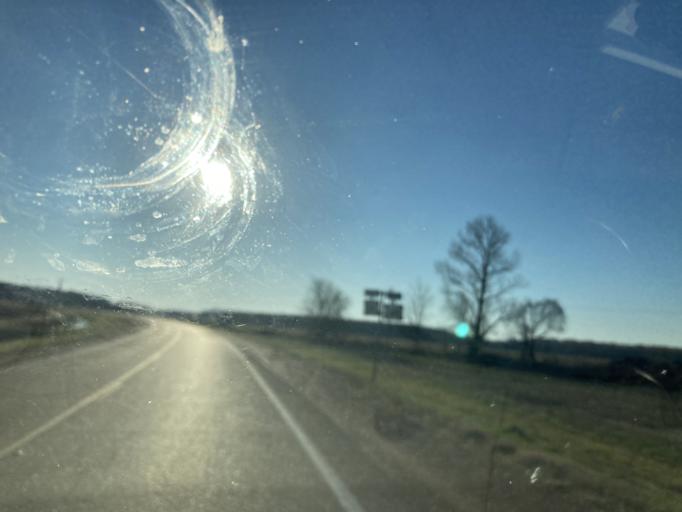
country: US
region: Mississippi
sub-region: Yazoo County
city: Yazoo City
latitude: 32.9282
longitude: -90.5840
